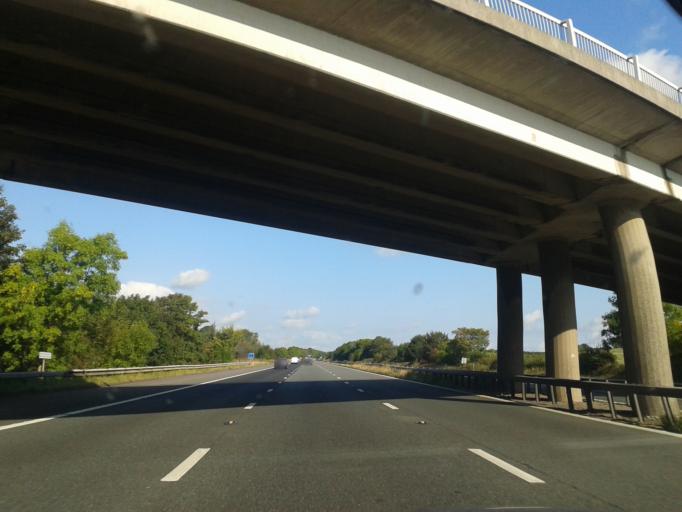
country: GB
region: England
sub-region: Lancashire
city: Carnforth
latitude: 54.1560
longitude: -2.7384
